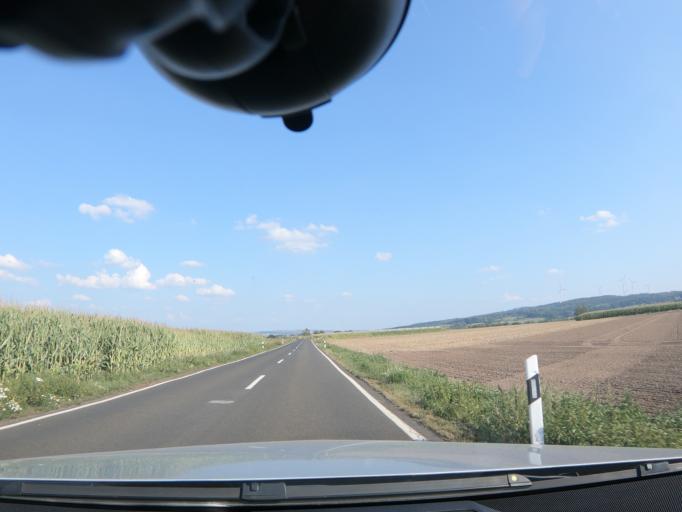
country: DE
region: Hesse
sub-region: Regierungsbezirk Giessen
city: Ebsdorfergrund
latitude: 50.7735
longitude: 8.8715
